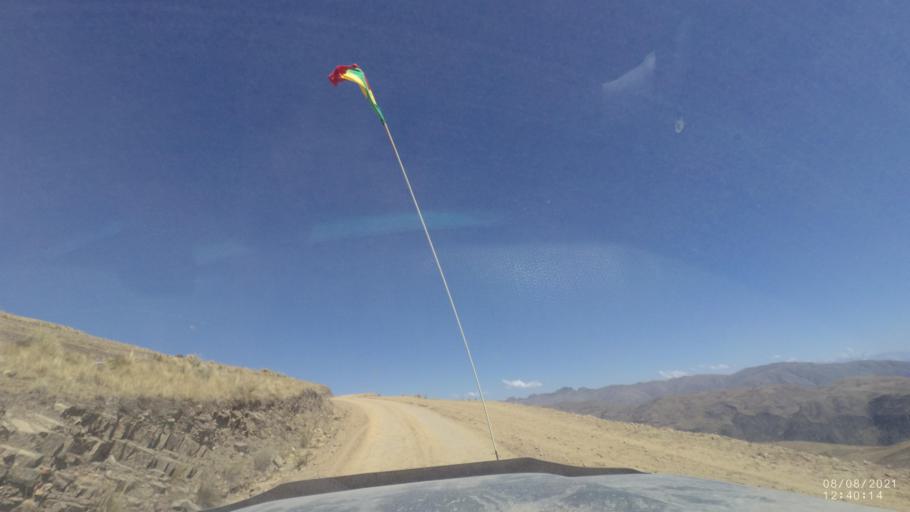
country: BO
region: Cochabamba
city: Colchani
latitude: -16.8270
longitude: -66.6228
